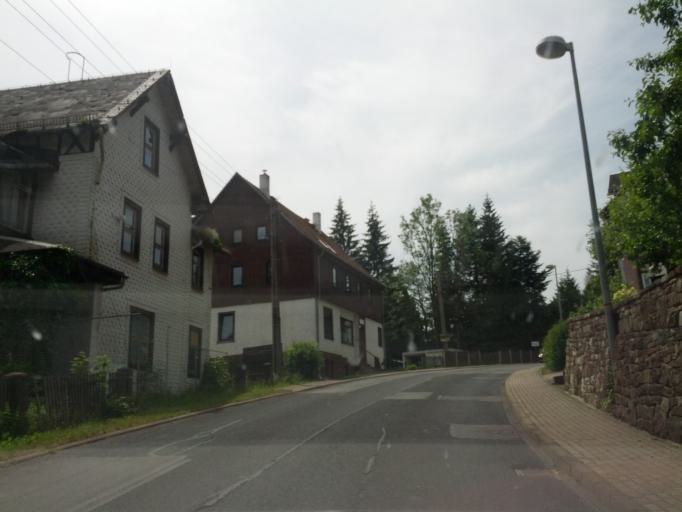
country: DE
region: Thuringia
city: Finsterbergen
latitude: 50.8381
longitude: 10.5961
